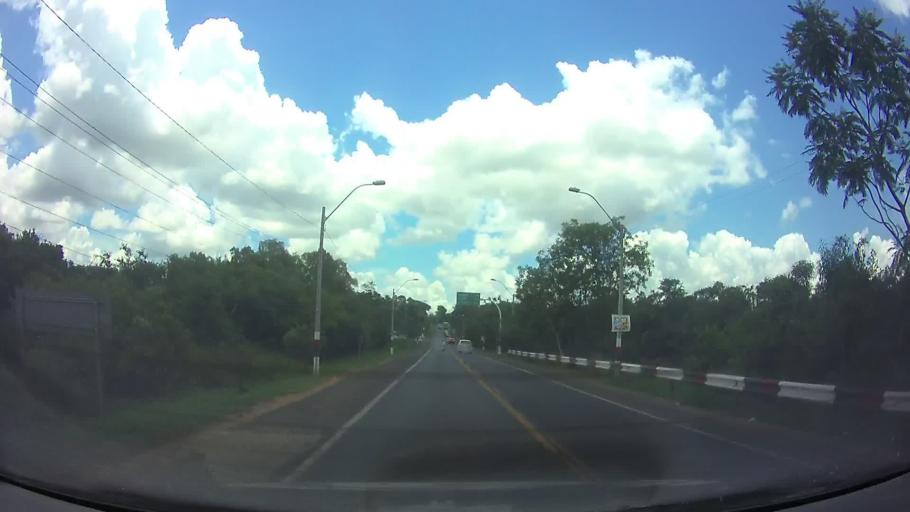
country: PY
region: Central
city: Capiata
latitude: -25.3474
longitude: -57.4164
